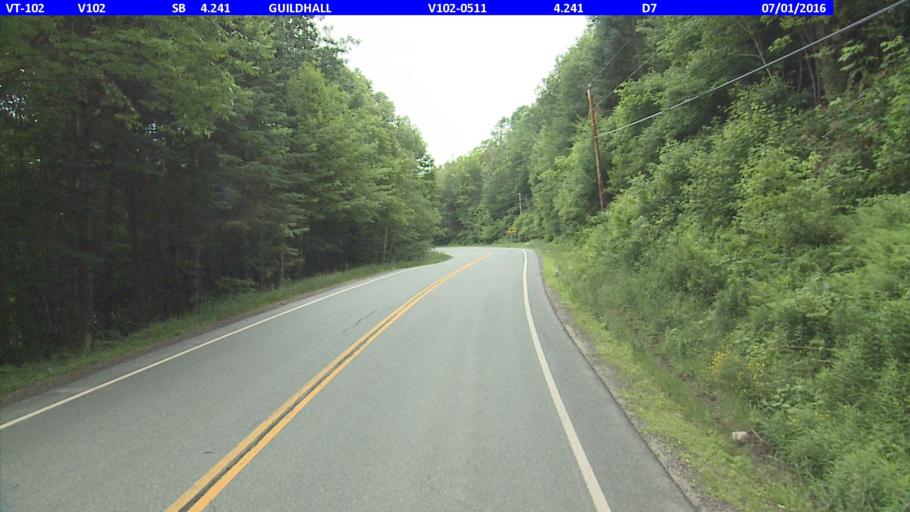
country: US
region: Vermont
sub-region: Essex County
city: Guildhall
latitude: 44.5501
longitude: -71.5926
